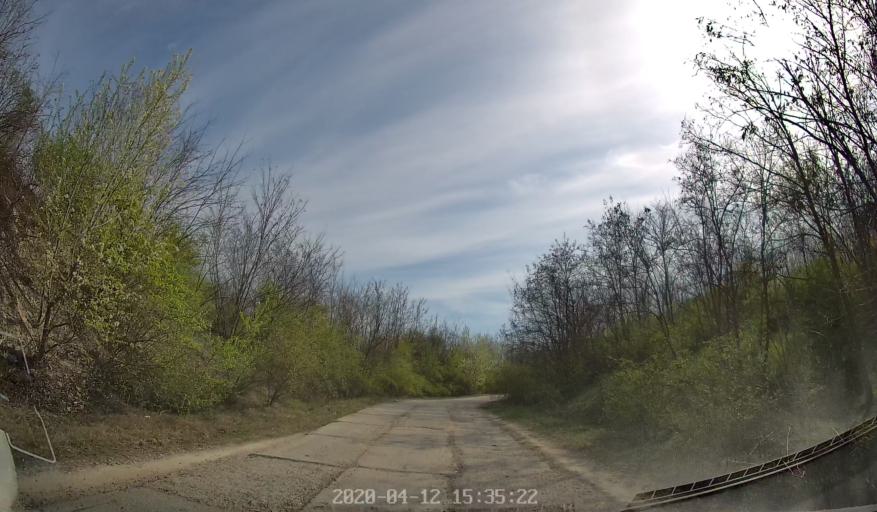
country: MD
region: Telenesti
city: Cocieri
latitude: 47.3260
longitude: 29.0710
